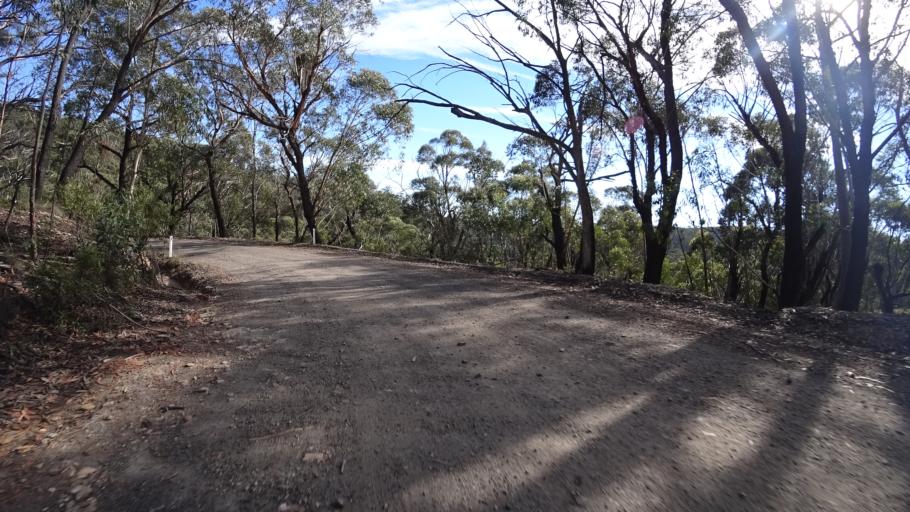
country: AU
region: New South Wales
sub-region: Lithgow
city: Lithgow
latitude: -33.5013
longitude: 150.1698
